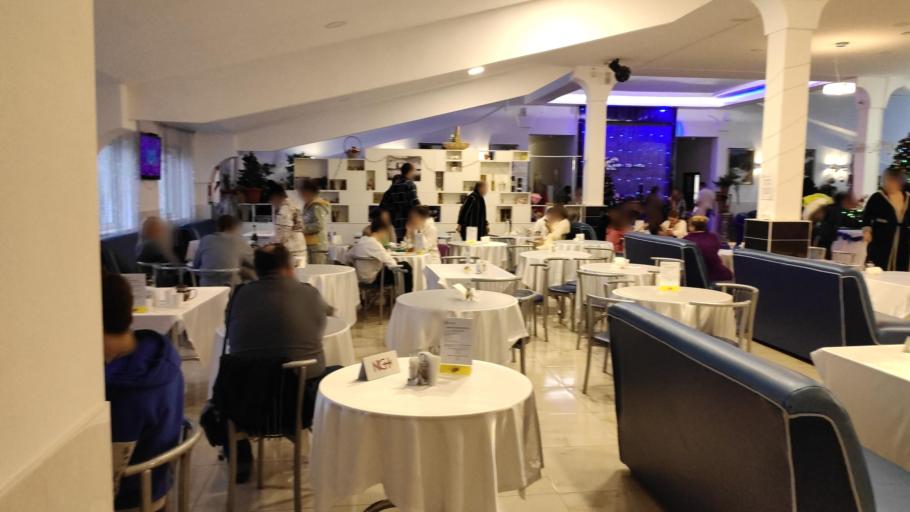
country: RU
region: Krasnodarskiy
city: Yaroslavskaya
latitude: 44.6050
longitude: 40.4433
